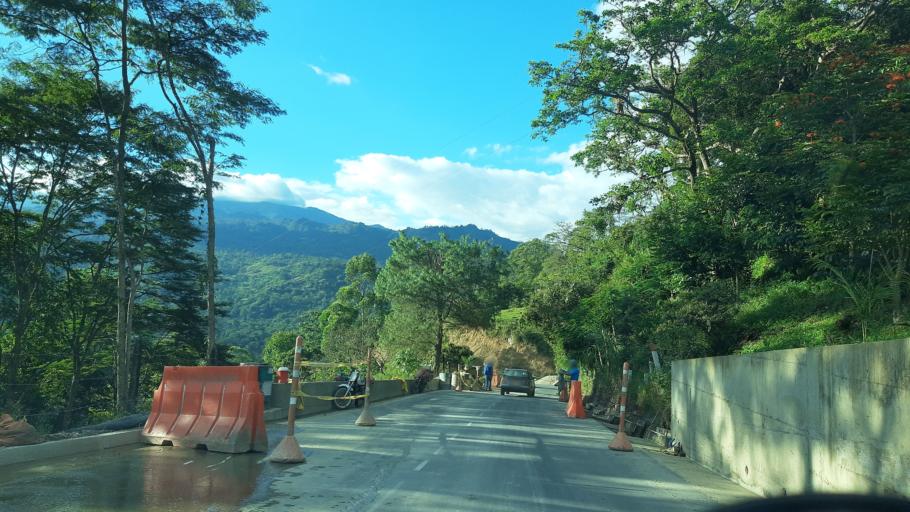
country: CO
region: Boyaca
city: Garagoa
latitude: 5.0764
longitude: -73.3800
